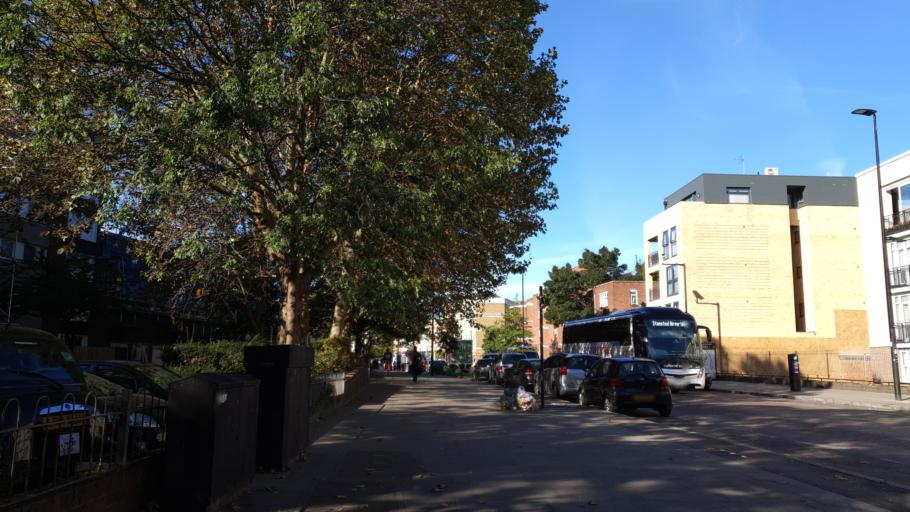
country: GB
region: England
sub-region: Greater London
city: Bethnal Green
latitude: 51.5259
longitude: -0.0683
